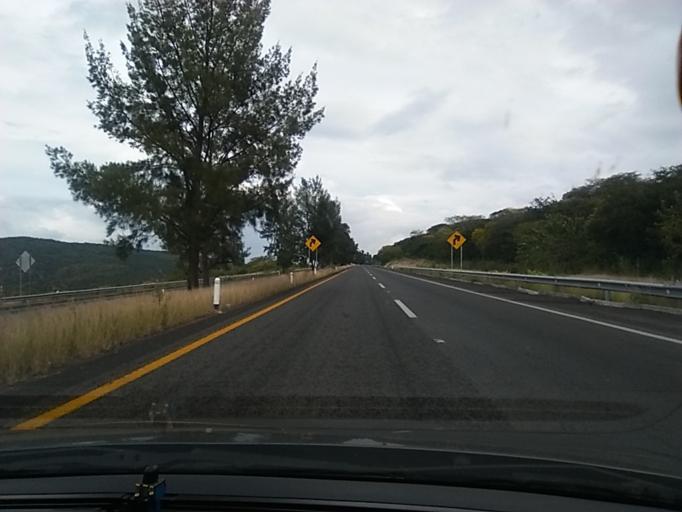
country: MX
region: Michoacan
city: Ixtlan
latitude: 20.2029
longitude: -102.3426
